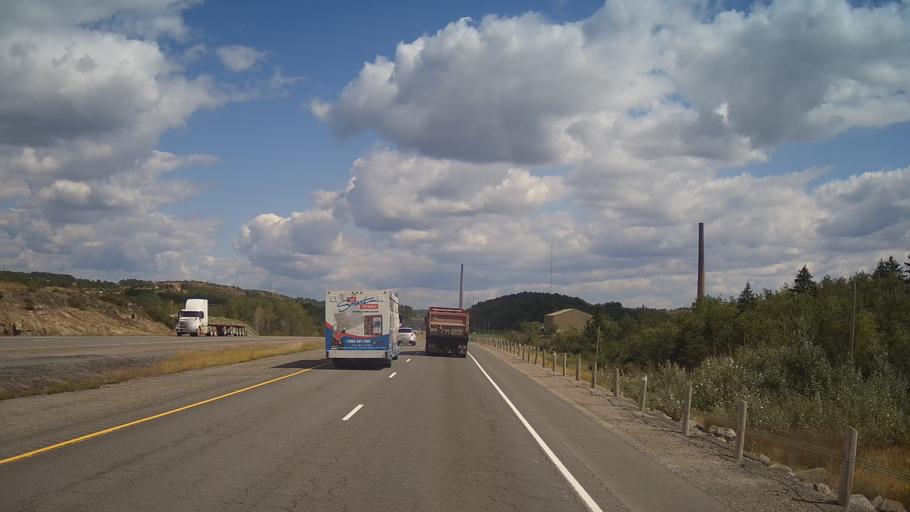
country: CA
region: Ontario
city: Greater Sudbury
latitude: 46.4388
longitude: -81.1072
